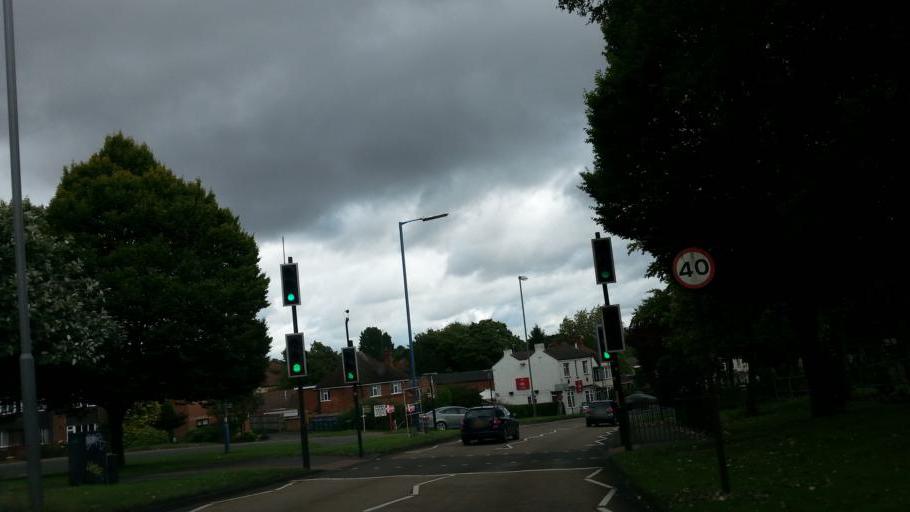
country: GB
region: England
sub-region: City and Borough of Birmingham
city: Bartley Green
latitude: 52.4633
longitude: -2.0027
